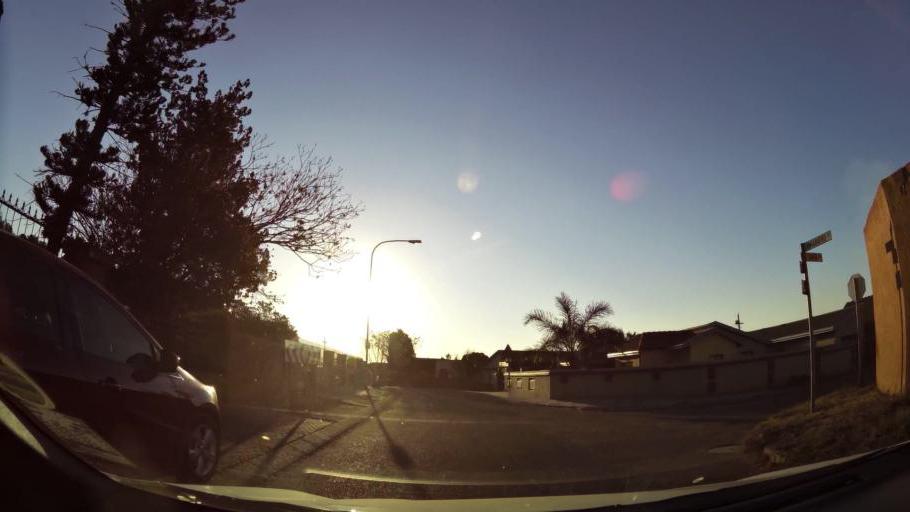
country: ZA
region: Gauteng
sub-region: City of Tshwane Metropolitan Municipality
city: Cullinan
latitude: -25.7262
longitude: 28.3907
